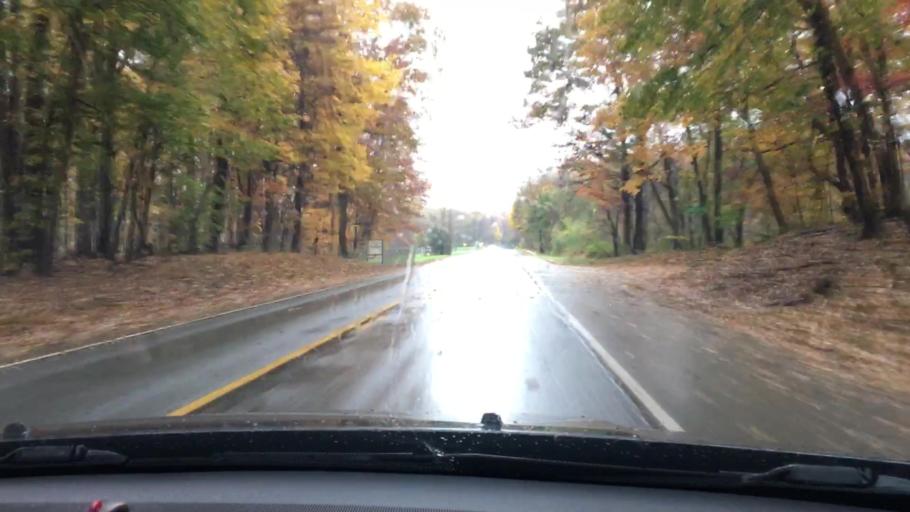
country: US
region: Pennsylvania
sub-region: York County
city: Susquehanna Trails
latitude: 39.8328
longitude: -76.3100
